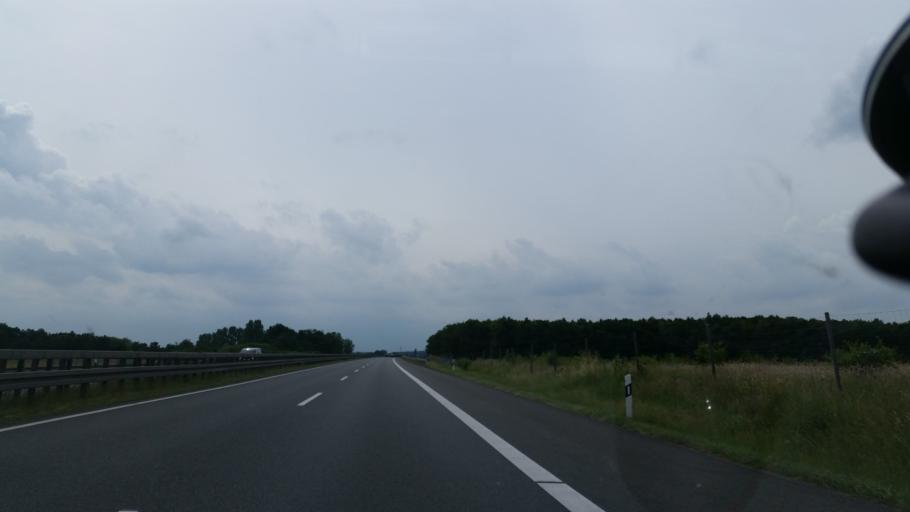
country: DE
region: Lower Saxony
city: Erkerode
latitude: 52.2814
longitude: 10.7104
